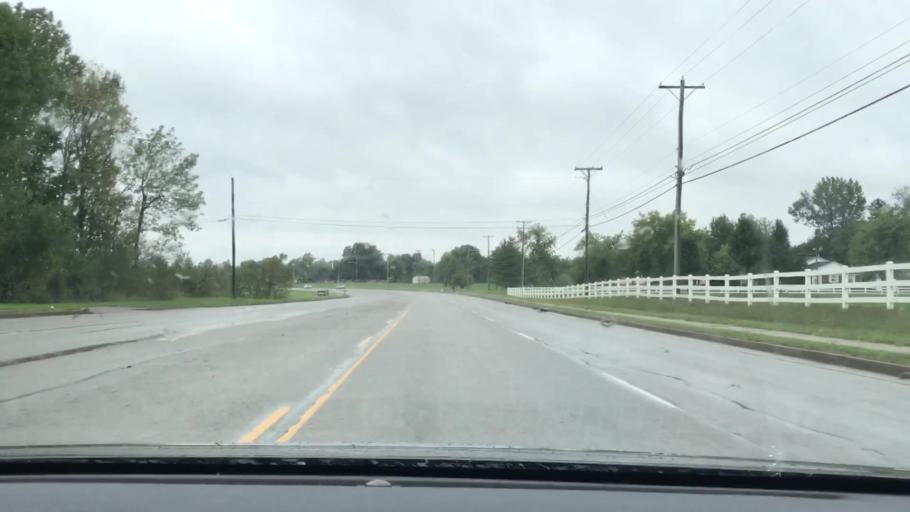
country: US
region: Kentucky
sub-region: Hopkins County
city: Madisonville
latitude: 37.3267
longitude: -87.4649
